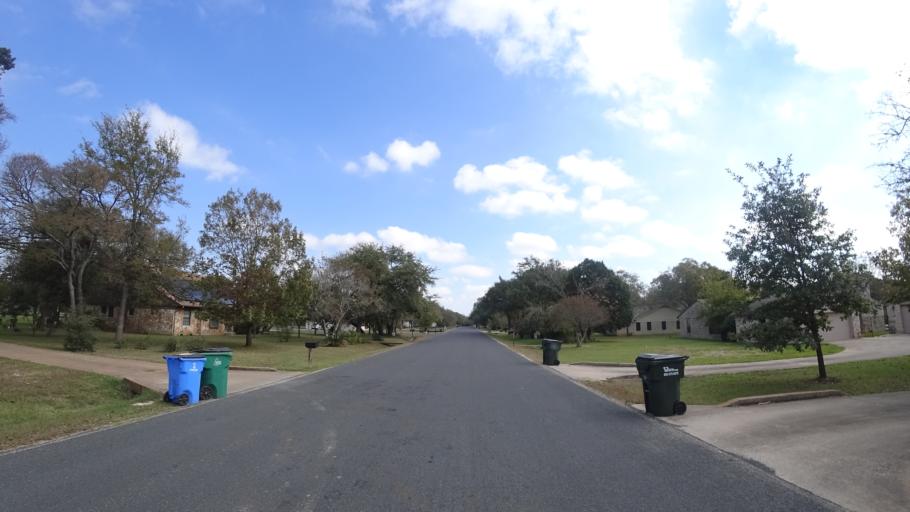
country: US
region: Texas
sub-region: Travis County
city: Shady Hollow
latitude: 30.1616
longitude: -97.8583
